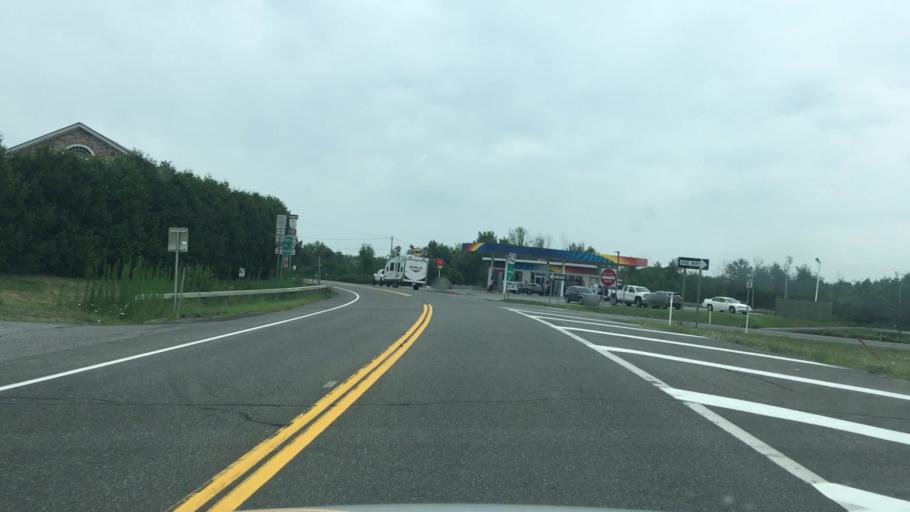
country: US
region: New York
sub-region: Essex County
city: Keeseville
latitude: 44.4956
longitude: -73.4982
